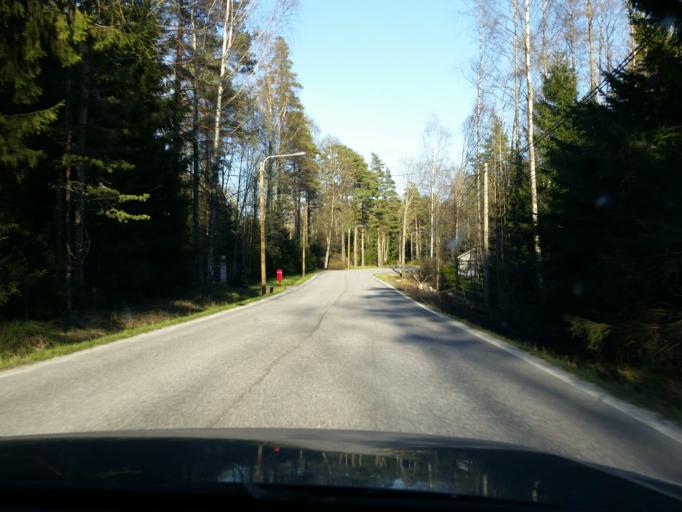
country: FI
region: Uusimaa
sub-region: Helsinki
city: Kirkkonummi
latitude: 60.1203
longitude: 24.5365
